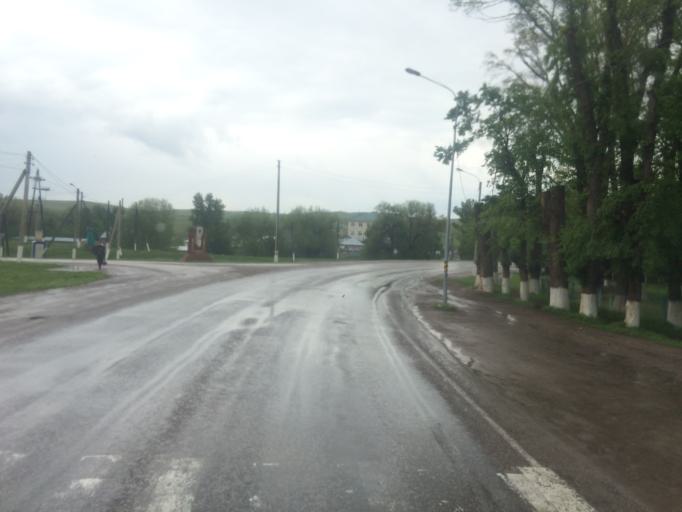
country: KZ
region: Zhambyl
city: Georgiyevka
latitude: 43.2344
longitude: 74.7593
